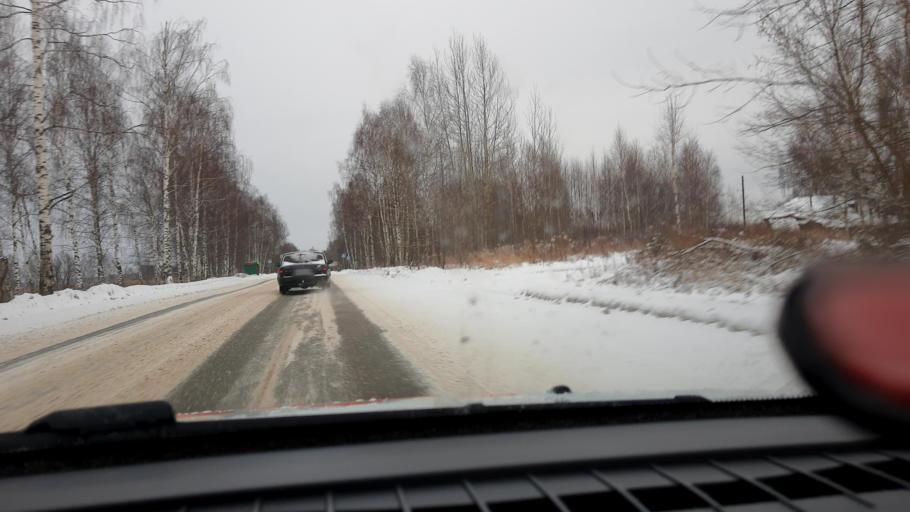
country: RU
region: Nizjnij Novgorod
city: Pamyat' Parizhskoy Kommuny
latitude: 56.2672
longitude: 44.4305
